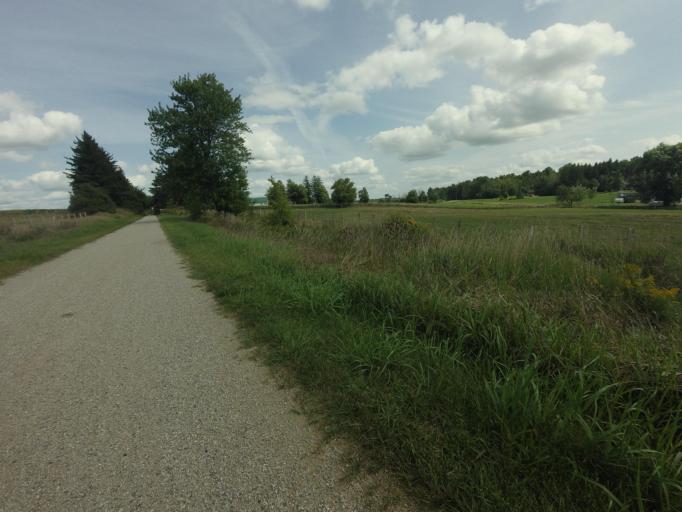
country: CA
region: Ontario
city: Waterloo
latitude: 43.5925
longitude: -80.6824
